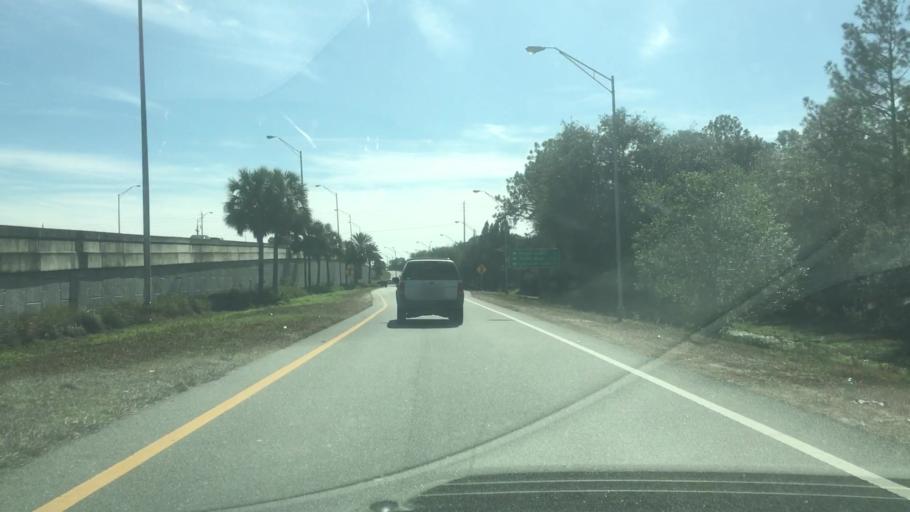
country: US
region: Florida
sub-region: Duval County
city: Jacksonville
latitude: 30.3264
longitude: -81.5287
